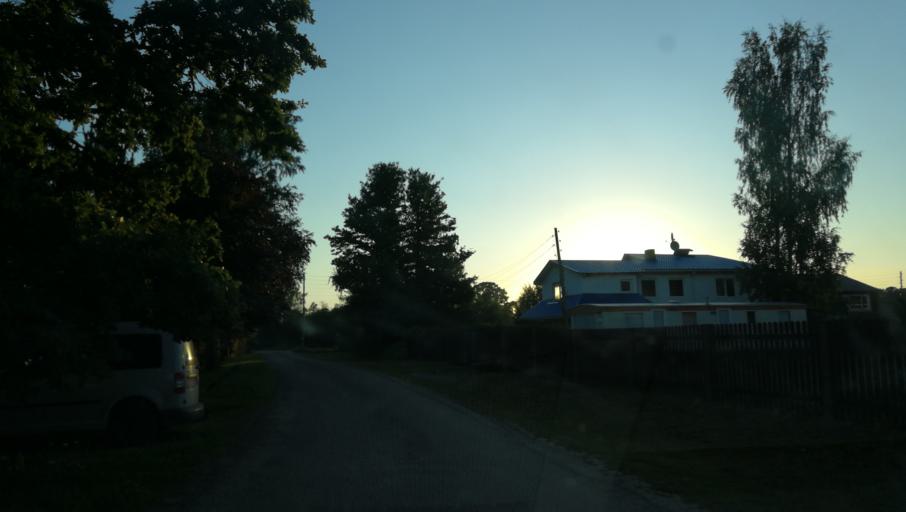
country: LV
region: Saulkrastu
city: Saulkrasti
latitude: 57.2992
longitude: 24.4146
